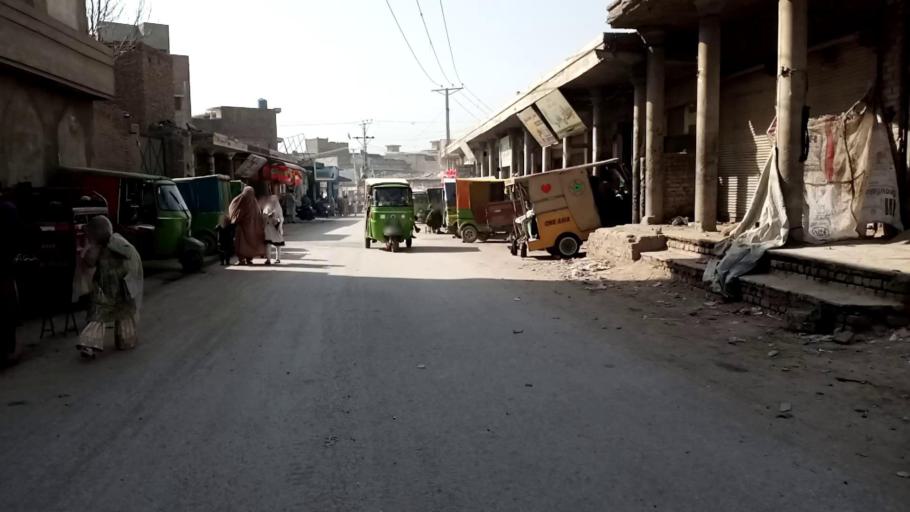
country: PK
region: Khyber Pakhtunkhwa
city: Peshawar
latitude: 33.9929
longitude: 71.5841
